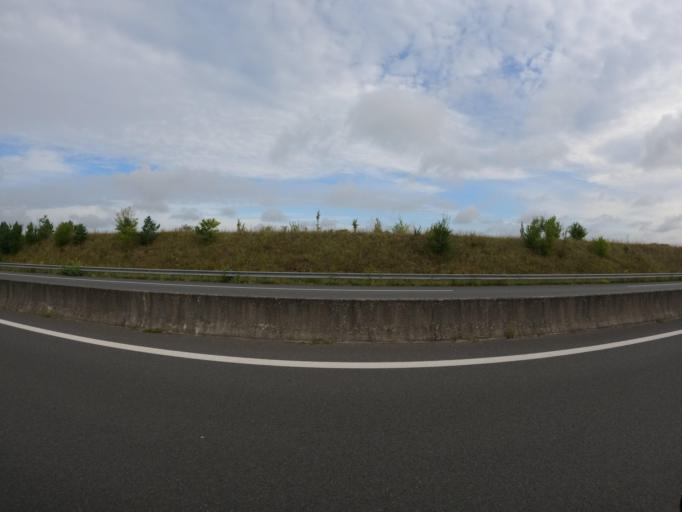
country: FR
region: Centre
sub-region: Departement d'Indre-et-Loire
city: Artannes-sur-Indre
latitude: 47.3077
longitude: 0.5841
